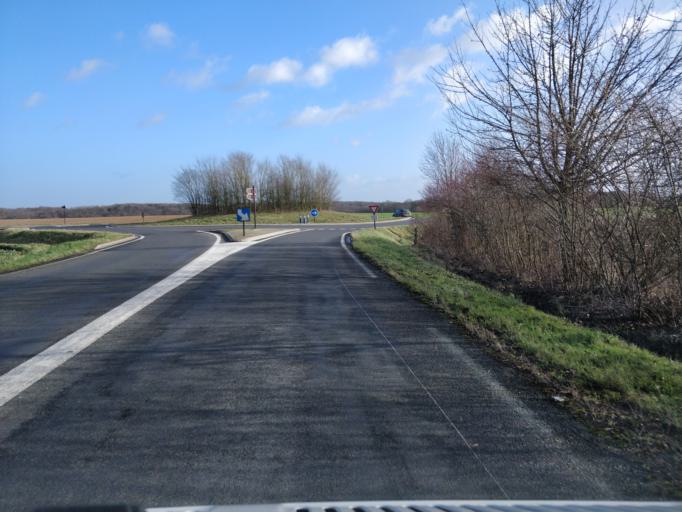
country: FR
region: Ile-de-France
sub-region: Departement de Seine-et-Marne
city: Lorrez-le-Bocage-Preaux
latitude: 48.2193
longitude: 2.8925
